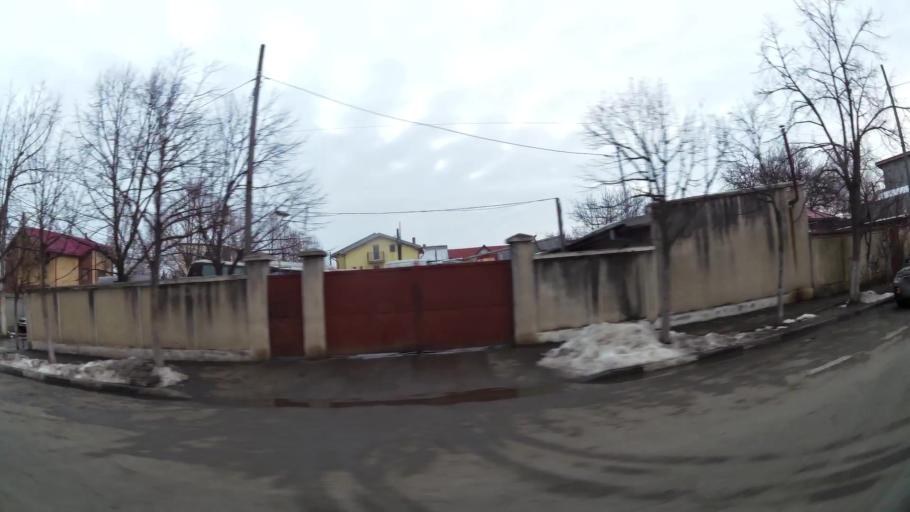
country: RO
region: Ilfov
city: Dobroesti
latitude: 44.4537
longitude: 26.1854
